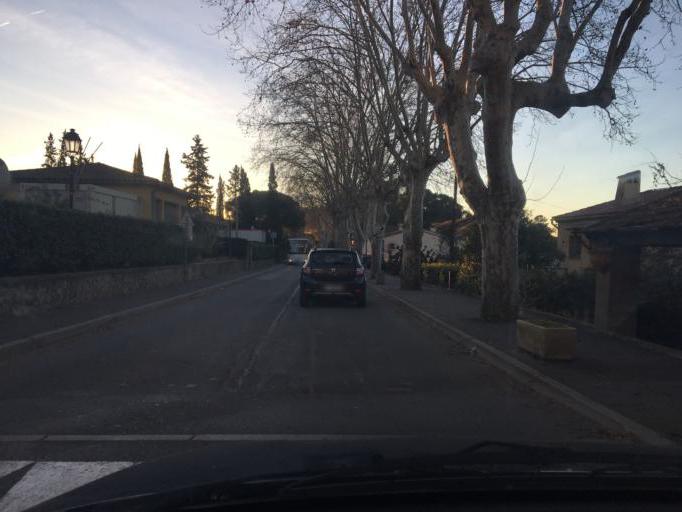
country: FR
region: Provence-Alpes-Cote d'Azur
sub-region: Departement du Var
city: Taradeau
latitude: 43.4539
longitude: 6.4277
